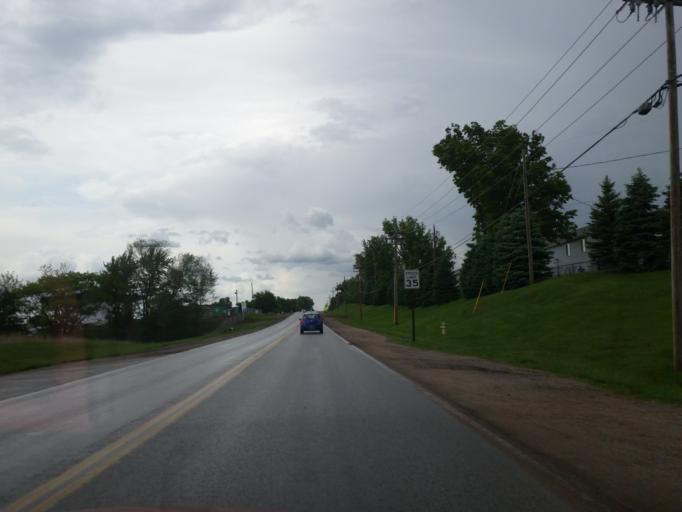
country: US
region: Nebraska
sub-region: Sarpy County
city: Offutt Air Force Base
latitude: 41.1220
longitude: -95.9665
